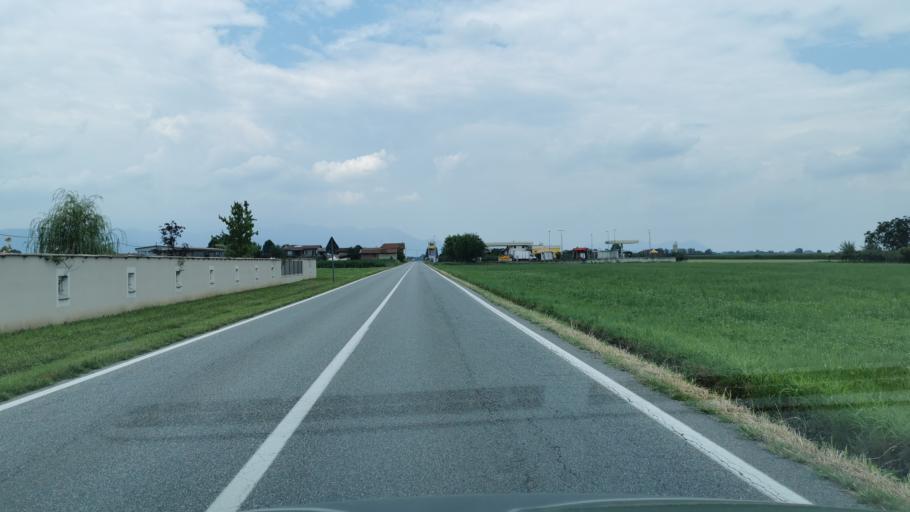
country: IT
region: Piedmont
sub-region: Provincia di Torino
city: Cavour
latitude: 44.8043
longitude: 7.3731
